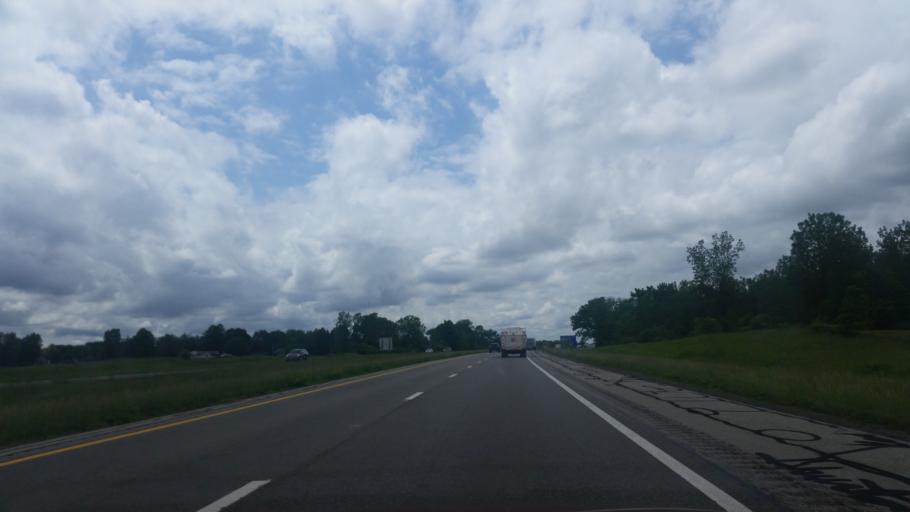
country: US
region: Ohio
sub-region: Crawford County
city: Galion
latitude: 40.7609
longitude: -82.7687
